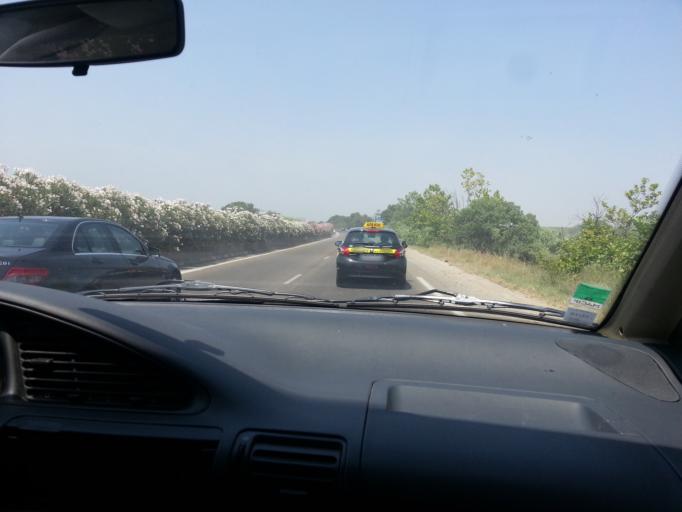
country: FR
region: Languedoc-Roussillon
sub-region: Departement de l'Herault
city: Perols
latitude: 43.5971
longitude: 3.9404
